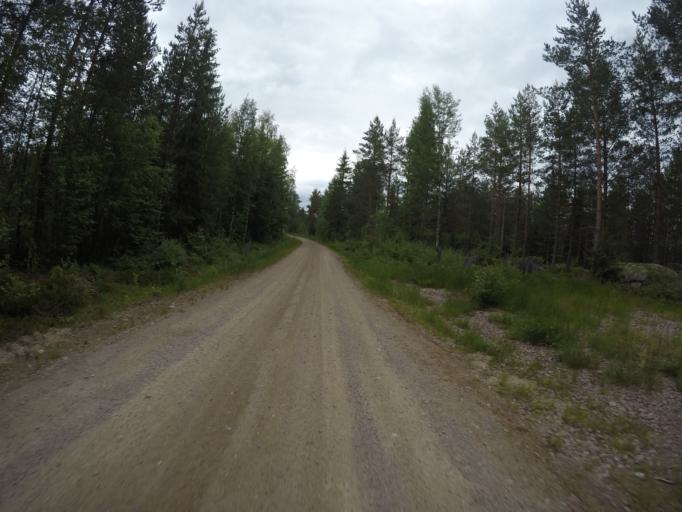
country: SE
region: Dalarna
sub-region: Ludvika Kommun
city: Abborrberget
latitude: 60.0866
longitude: 14.5510
